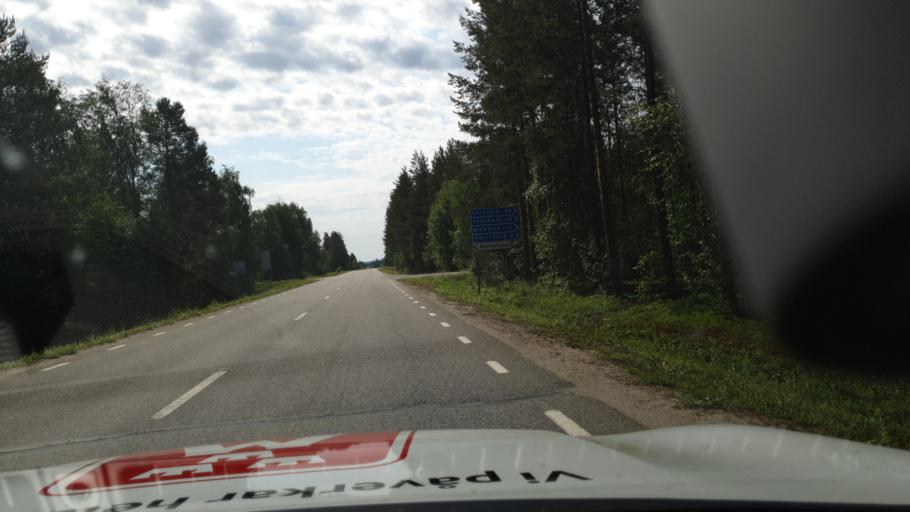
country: SE
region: Vaesterbotten
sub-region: Norsjo Kommun
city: Norsjoe
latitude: 64.5803
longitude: 19.3027
